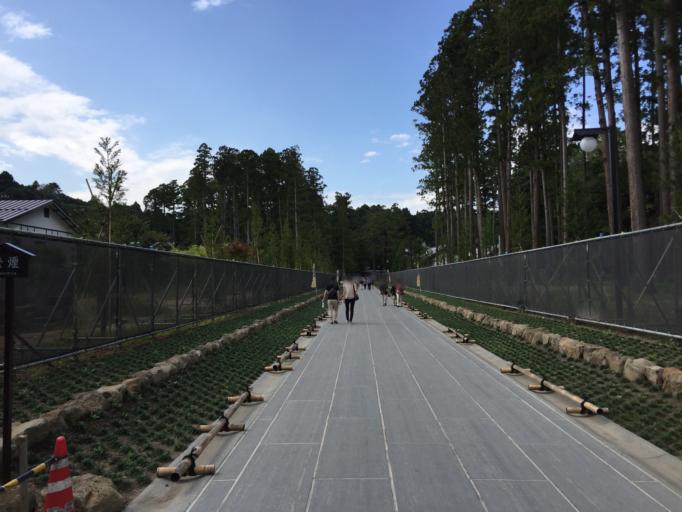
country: JP
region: Miyagi
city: Matsushima
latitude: 38.3704
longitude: 141.0623
